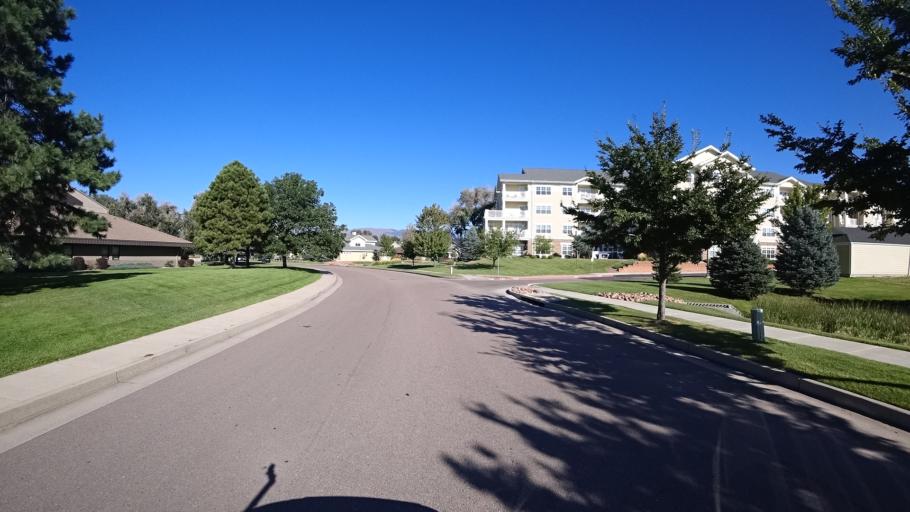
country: US
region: Colorado
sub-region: El Paso County
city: Colorado Springs
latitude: 38.8713
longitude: -104.7973
